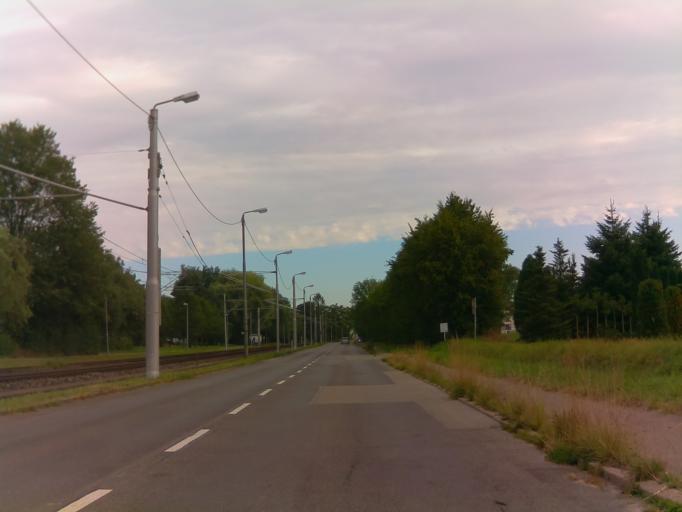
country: DE
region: Baden-Wuerttemberg
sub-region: Regierungsbezirk Stuttgart
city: Leinfelden-Echterdingen
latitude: 48.7370
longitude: 9.1517
